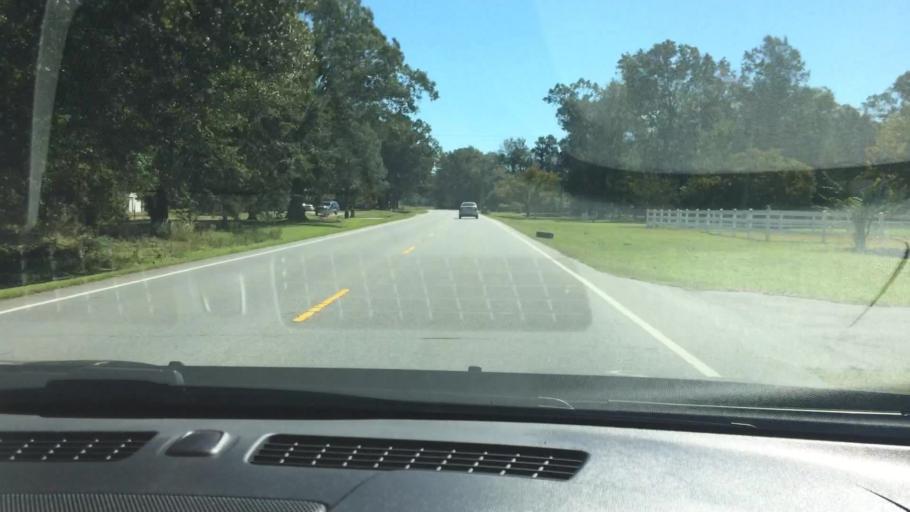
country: US
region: North Carolina
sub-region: Pitt County
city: Grifton
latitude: 35.3551
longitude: -77.3386
